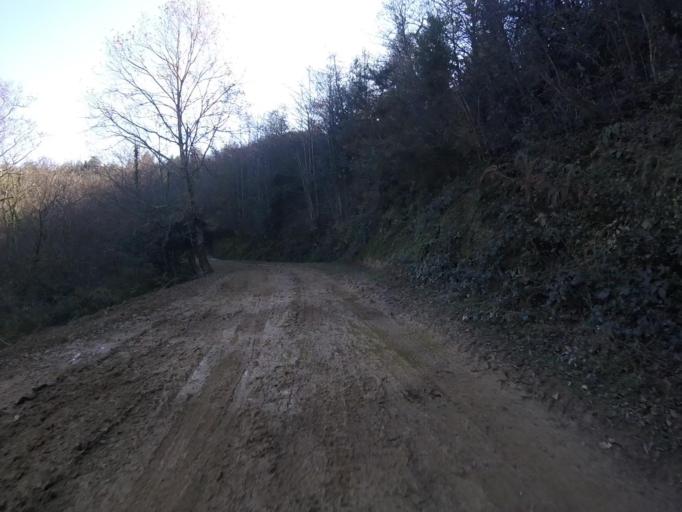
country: ES
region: Navarre
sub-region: Provincia de Navarra
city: Bera
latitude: 43.3163
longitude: -1.7136
